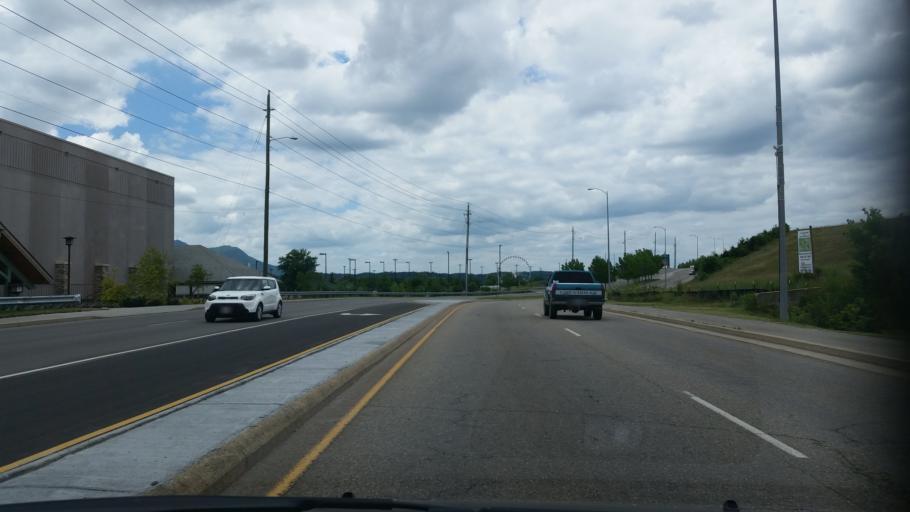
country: US
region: Tennessee
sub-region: Sevier County
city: Pigeon Forge
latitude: 35.7981
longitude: -83.5612
